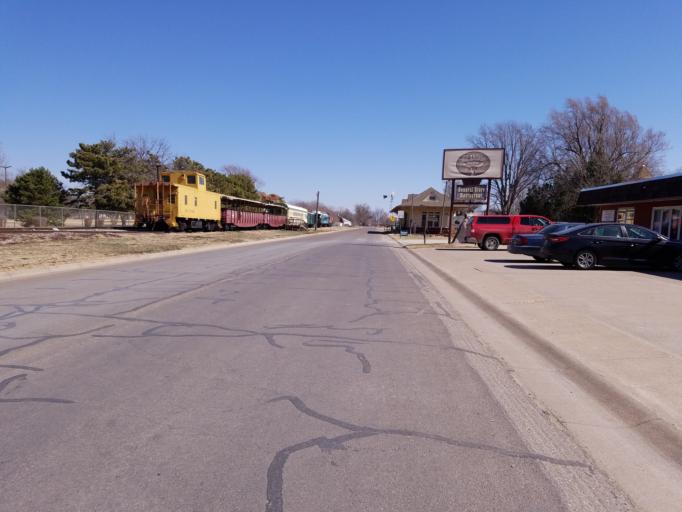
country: US
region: Kansas
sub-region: Dickinson County
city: Abilene
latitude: 38.9109
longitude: -97.2134
